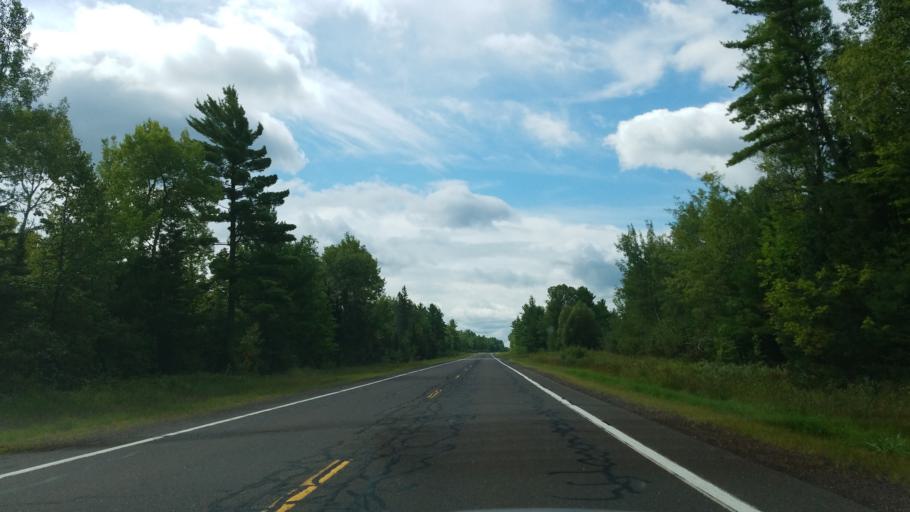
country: US
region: Michigan
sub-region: Ontonagon County
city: Ontonagon
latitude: 46.6564
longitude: -89.1730
